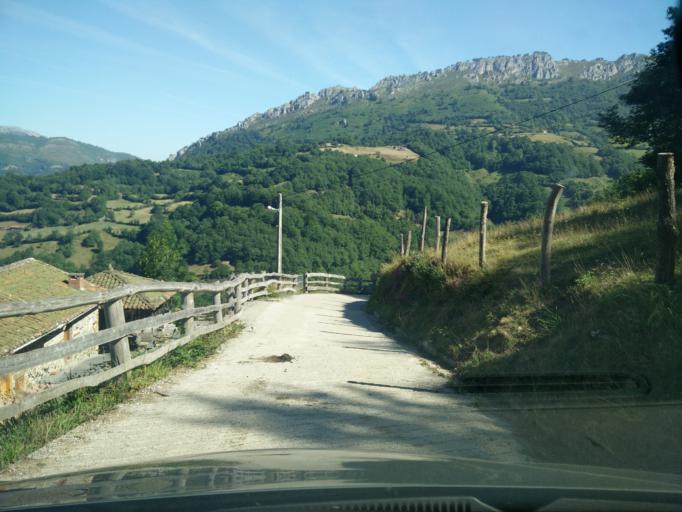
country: ES
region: Asturias
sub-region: Province of Asturias
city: Campo de Caso
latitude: 43.1468
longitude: -5.3788
